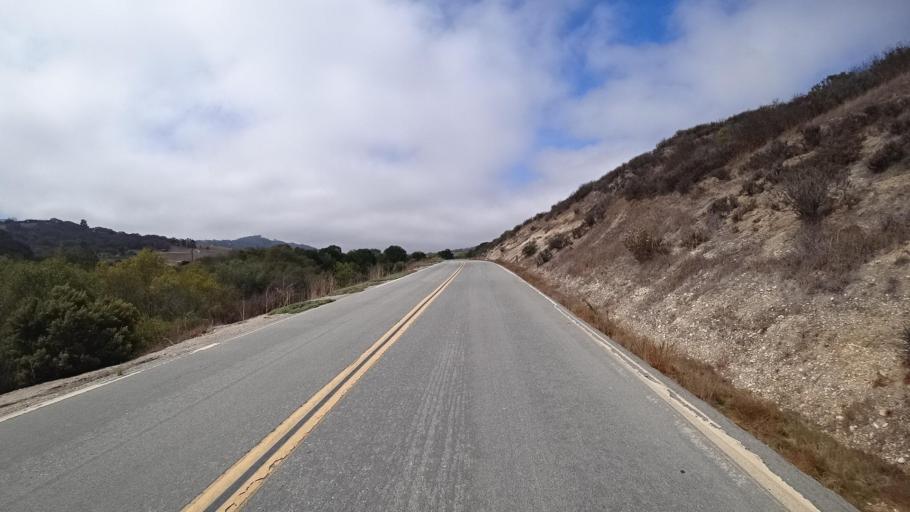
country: US
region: California
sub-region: Monterey County
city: Carmel Valley Village
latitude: 36.5717
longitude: -121.7642
